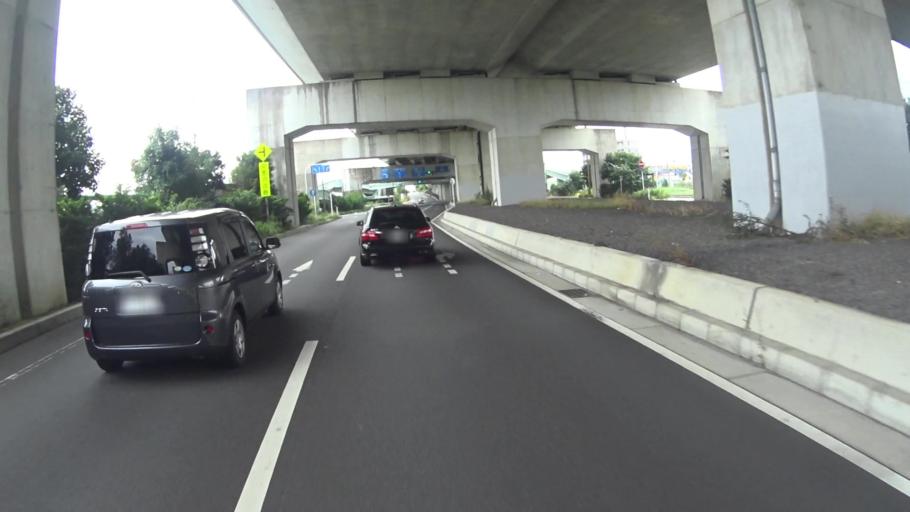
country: JP
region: Kyoto
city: Yawata
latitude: 34.8762
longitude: 135.7481
